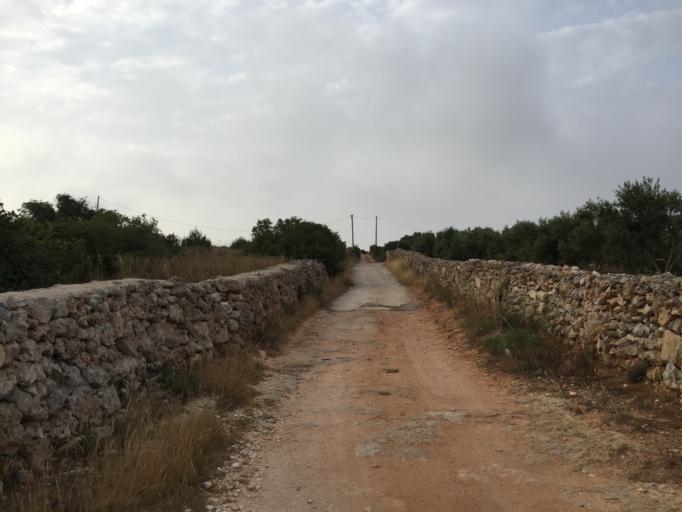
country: MT
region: L-Imgarr
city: Imgarr
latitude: 35.9338
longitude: 14.3858
